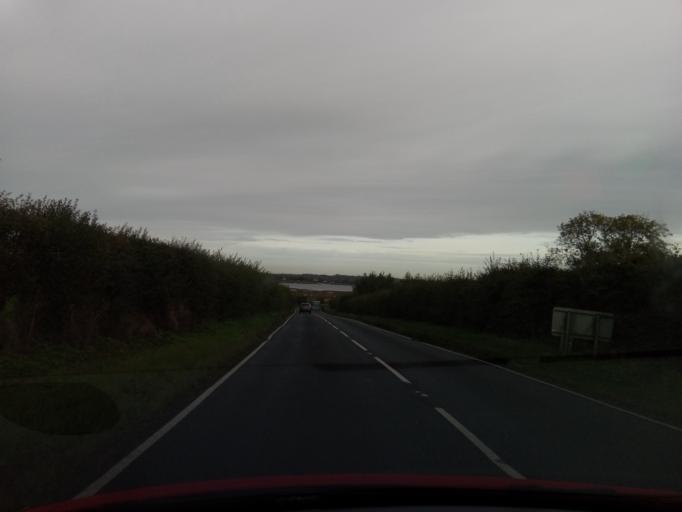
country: GB
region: England
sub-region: Essex
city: West Mersea
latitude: 51.7889
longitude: 0.9212
